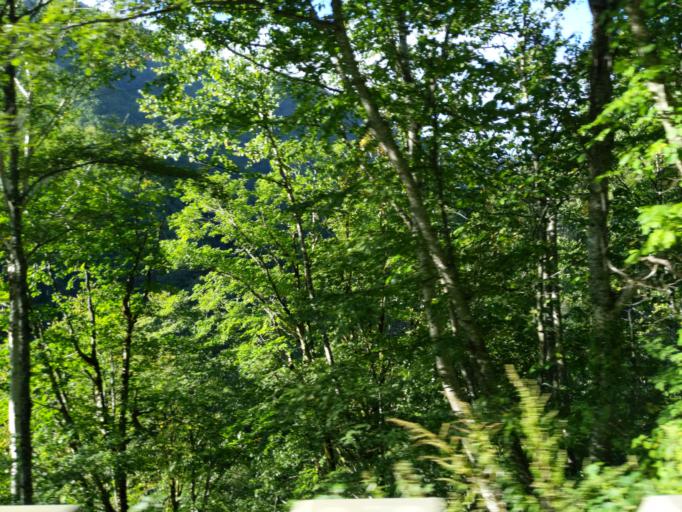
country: JP
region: Toyama
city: Kamiichi
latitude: 36.5101
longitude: 137.4499
